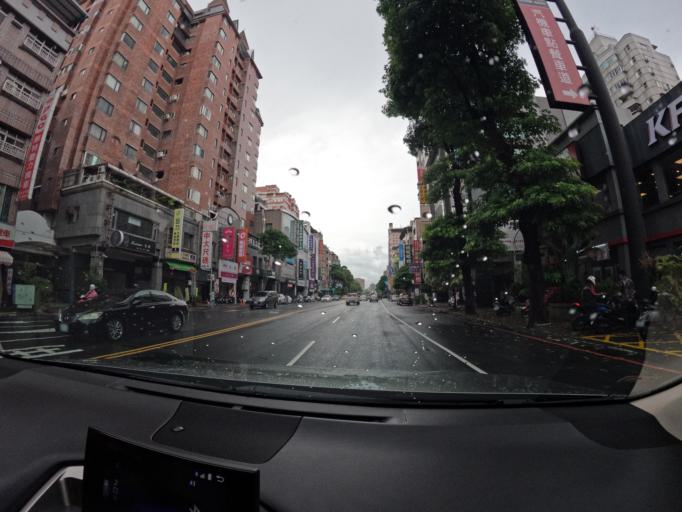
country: TW
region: Kaohsiung
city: Kaohsiung
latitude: 22.6607
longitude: 120.3087
